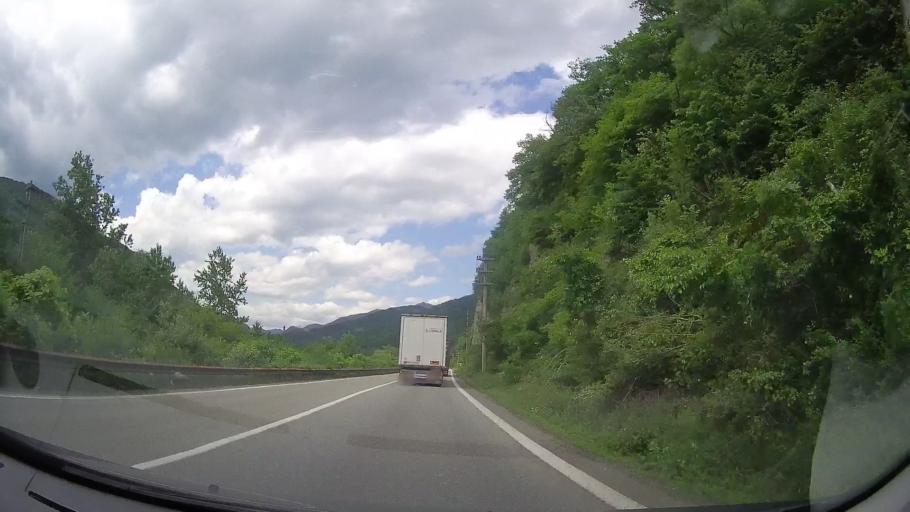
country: RO
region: Valcea
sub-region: Oras Calimanesti
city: Jiblea Veche
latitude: 45.2505
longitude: 24.3401
